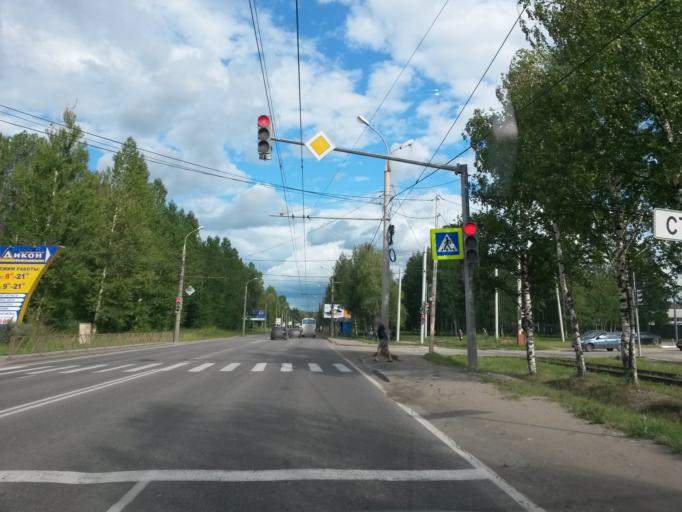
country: RU
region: Jaroslavl
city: Yaroslavl
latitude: 57.6765
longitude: 39.8059
